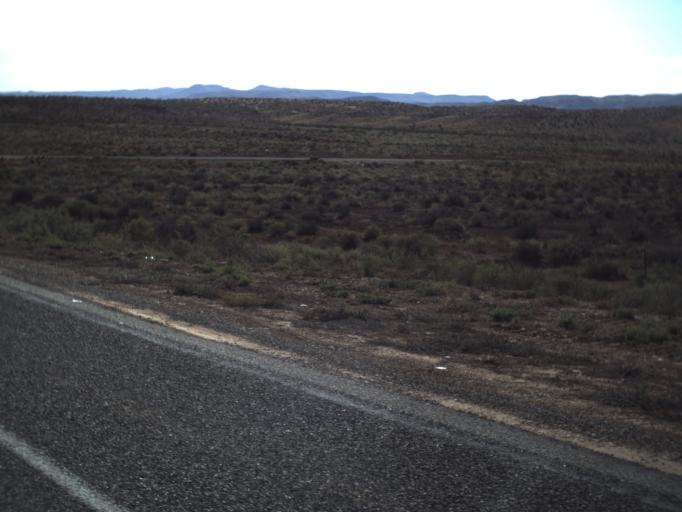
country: US
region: Utah
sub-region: Washington County
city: Saint George
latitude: 37.0003
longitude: -113.5620
